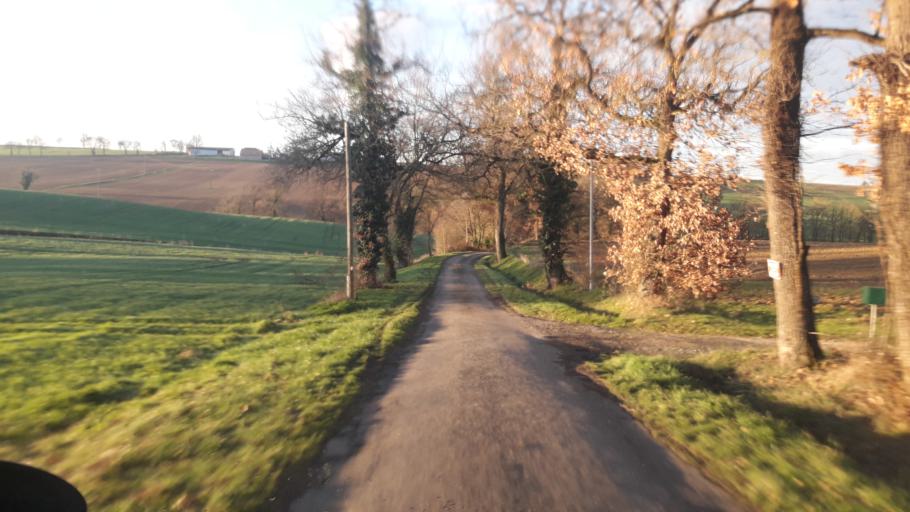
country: FR
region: Midi-Pyrenees
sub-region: Departement du Gers
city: Gimont
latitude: 43.6978
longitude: 0.9315
